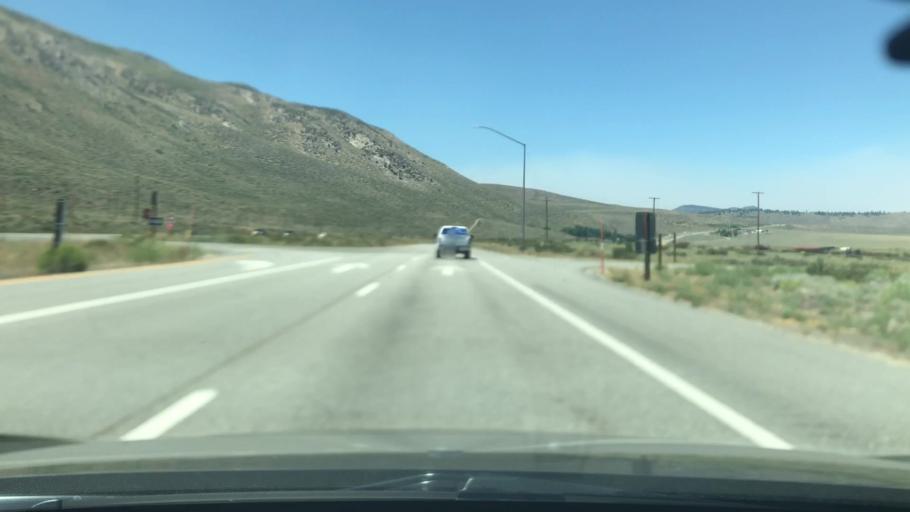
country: US
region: California
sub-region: Mono County
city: Mammoth Lakes
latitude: 37.5876
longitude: -118.7832
